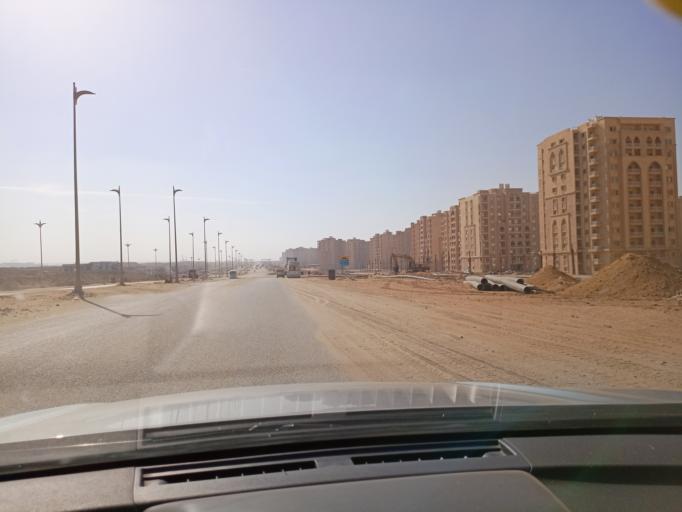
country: EG
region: Muhafazat al Qalyubiyah
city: Al Khankah
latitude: 30.0239
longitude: 31.6719
